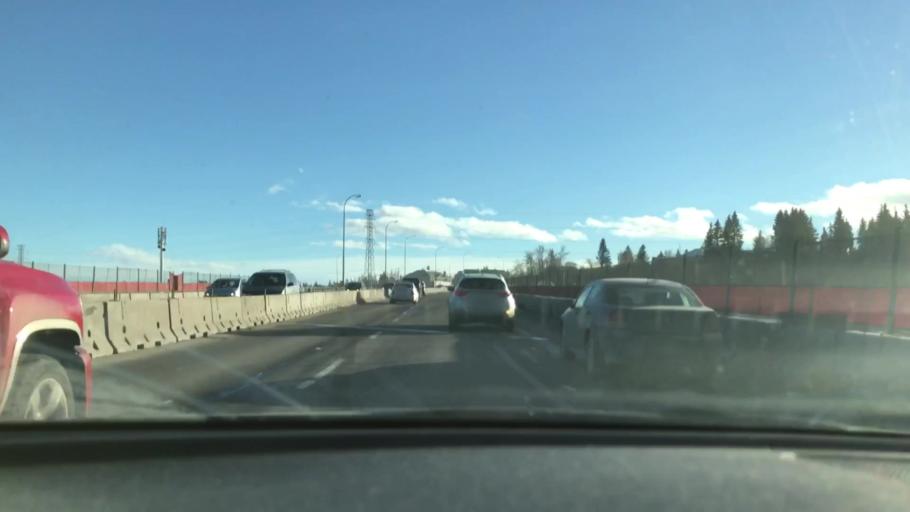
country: CA
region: Alberta
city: Calgary
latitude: 51.0477
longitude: -114.1156
